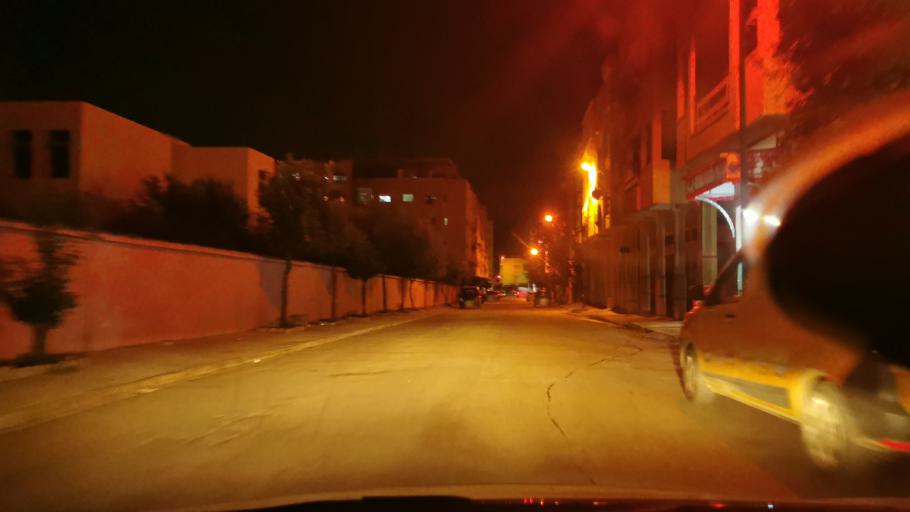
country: MA
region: Fes-Boulemane
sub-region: Fes
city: Fes
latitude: 34.0108
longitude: -4.9692
